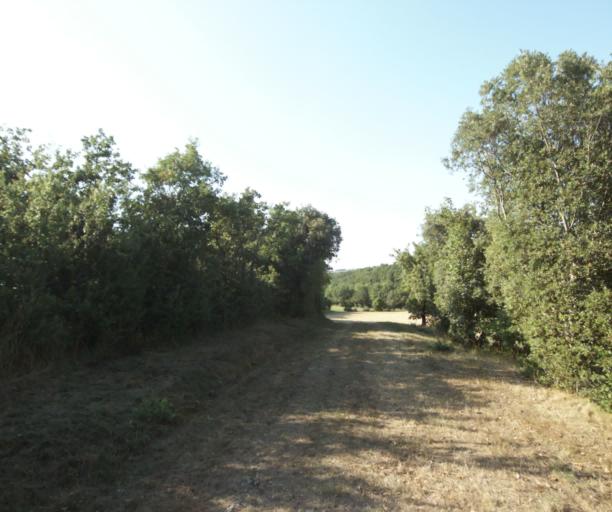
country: FR
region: Midi-Pyrenees
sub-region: Departement de la Haute-Garonne
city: Saint-Felix-Lauragais
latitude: 43.4311
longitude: 1.8263
